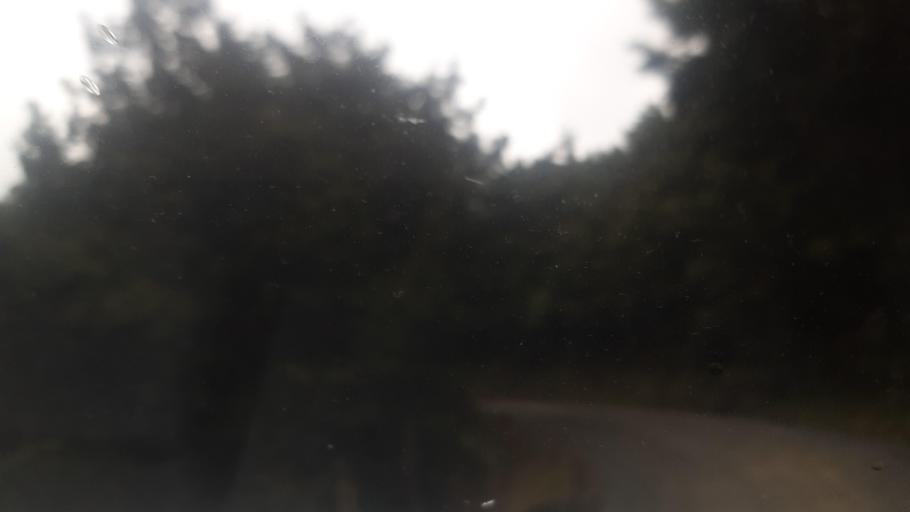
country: NZ
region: Northland
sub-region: Far North District
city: Taipa
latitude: -35.0514
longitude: 173.3918
